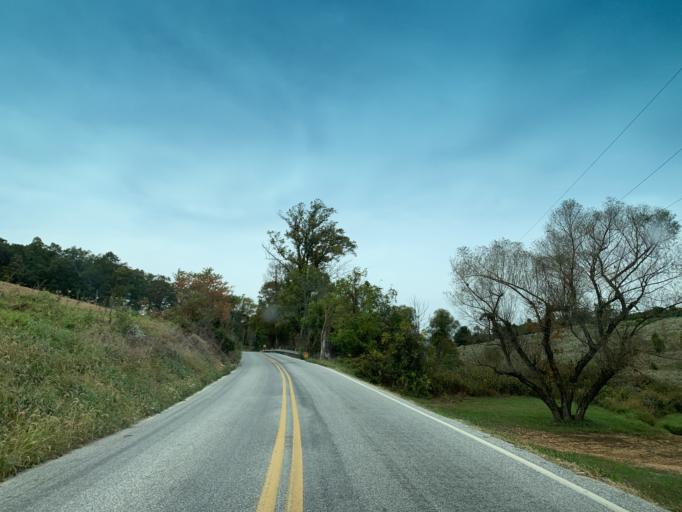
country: US
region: Pennsylvania
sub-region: York County
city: Windsor
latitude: 39.8496
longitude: -76.5111
